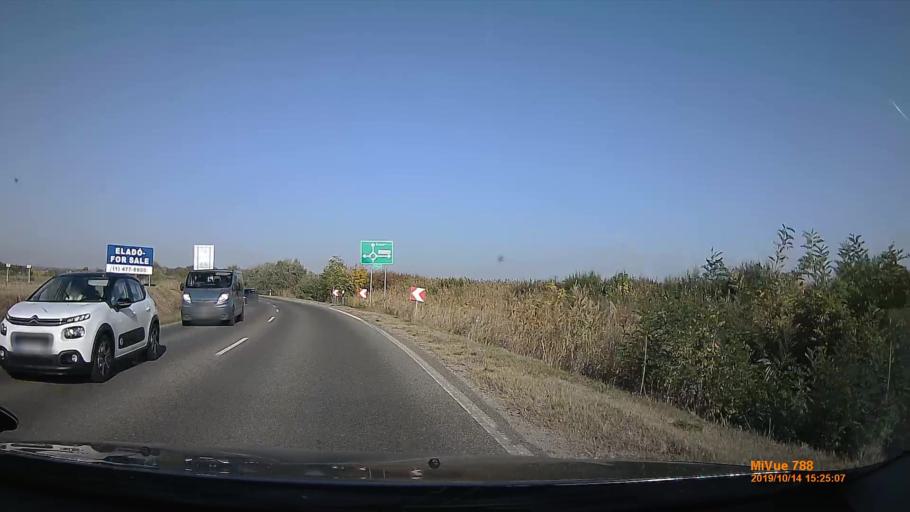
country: HU
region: Pest
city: Vecses
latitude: 47.4077
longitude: 19.3076
